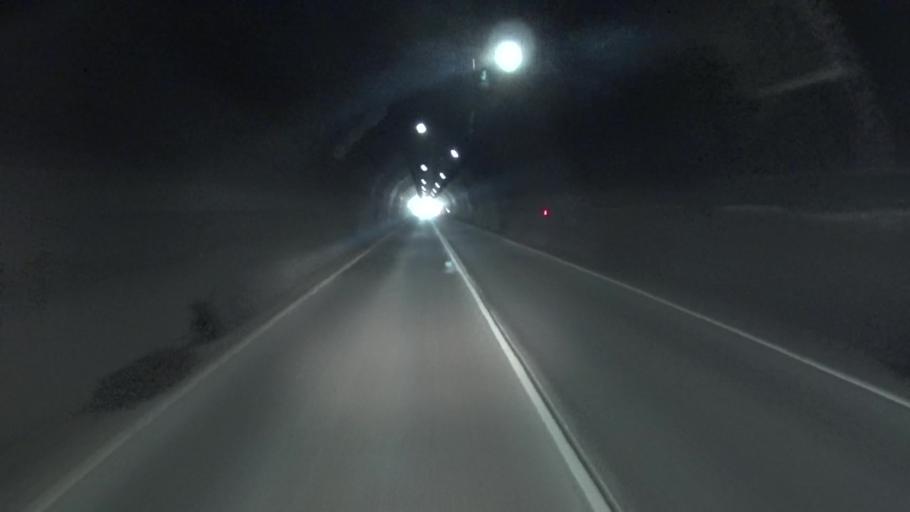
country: JP
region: Fukui
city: Obama
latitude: 35.4854
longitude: 135.7231
